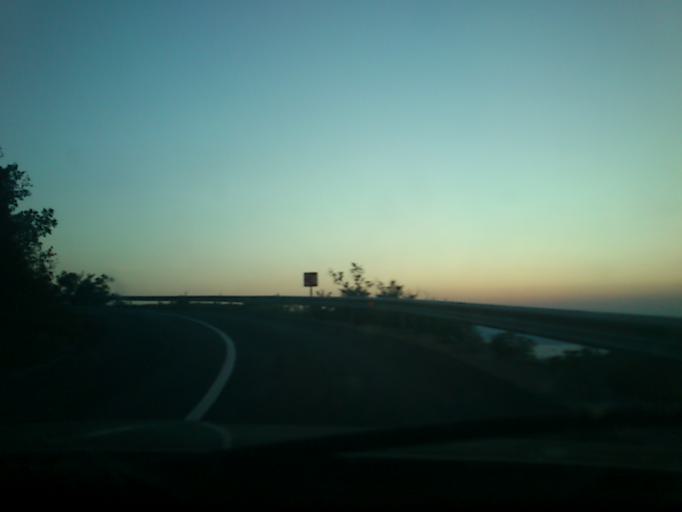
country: HR
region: Licko-Senjska
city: Senj
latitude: 44.9123
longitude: 14.9440
